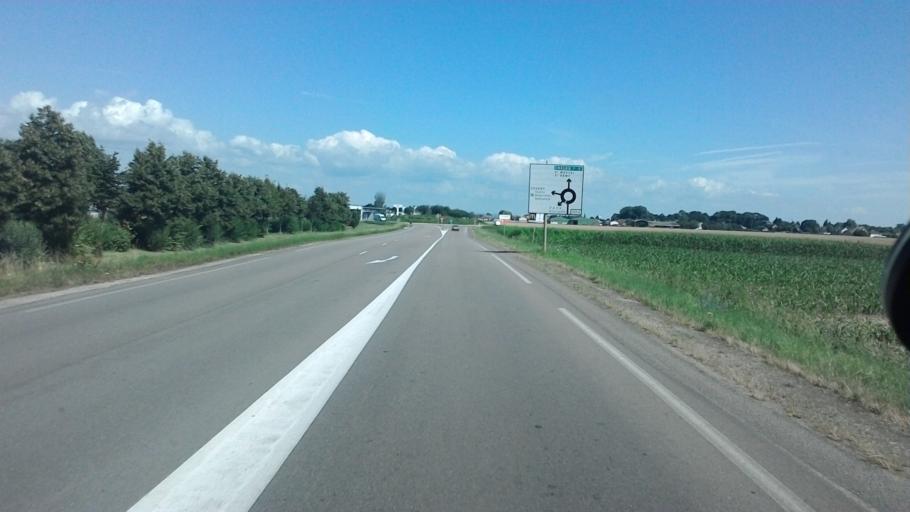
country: FR
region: Bourgogne
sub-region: Departement de Saone-et-Loire
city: Sevrey
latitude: 46.7407
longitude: 4.8539
